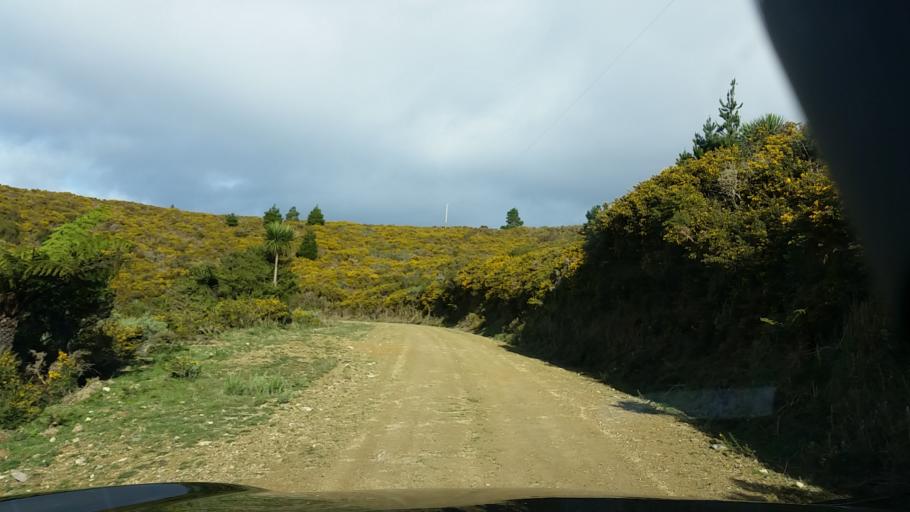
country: NZ
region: Marlborough
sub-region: Marlborough District
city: Picton
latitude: -40.9710
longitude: 173.8930
